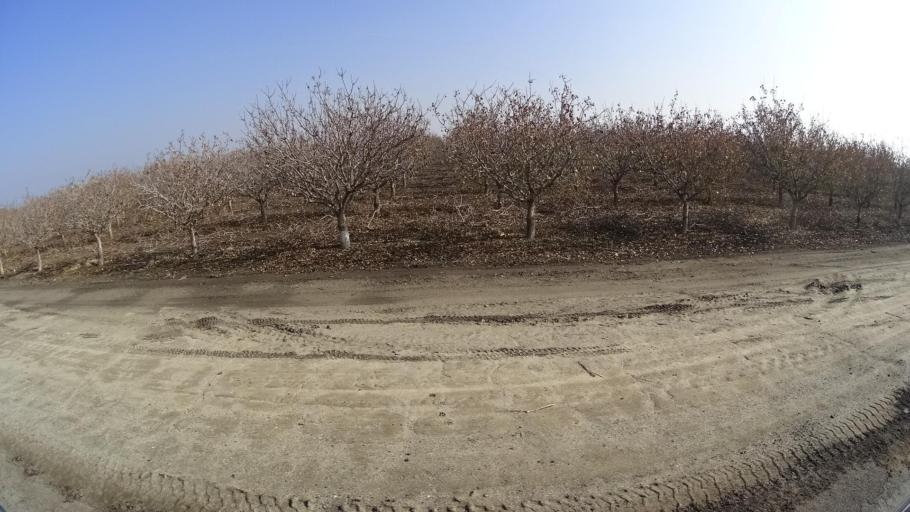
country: US
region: California
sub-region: Kern County
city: Buttonwillow
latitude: 35.3454
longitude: -119.3945
